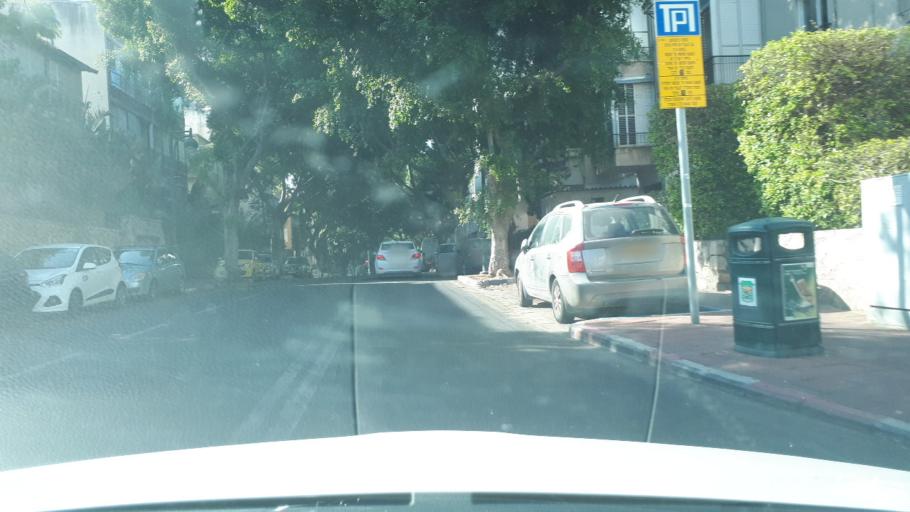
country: IL
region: Tel Aviv
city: Ramat Gan
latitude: 32.0804
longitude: 34.8199
